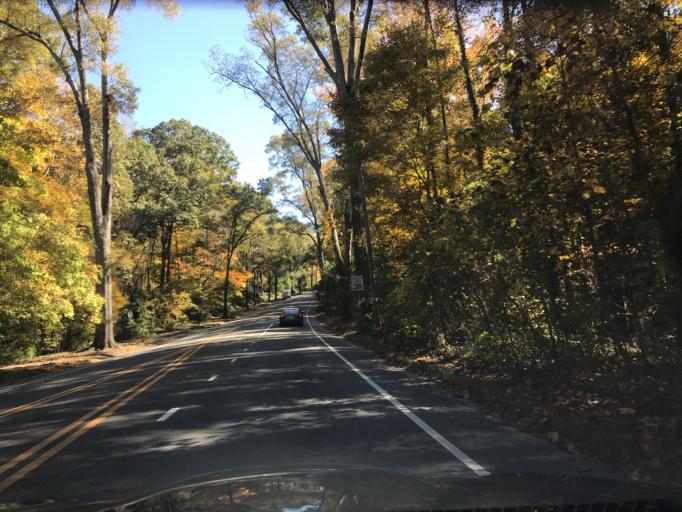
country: US
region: North Carolina
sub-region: Durham County
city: Durham
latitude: 35.9981
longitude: -78.9281
